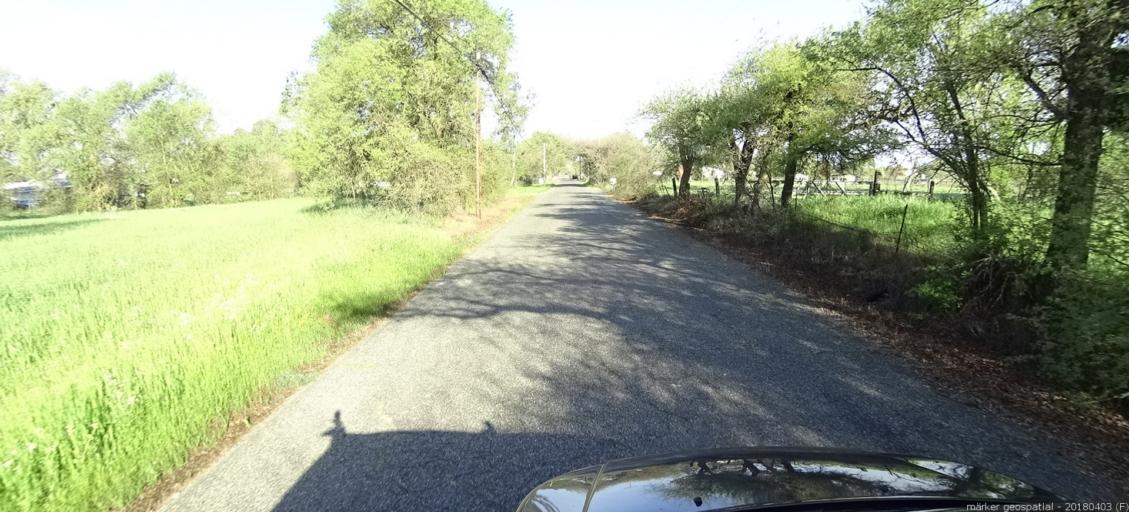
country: US
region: California
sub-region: Sacramento County
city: Wilton
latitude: 38.4400
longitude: -121.1939
